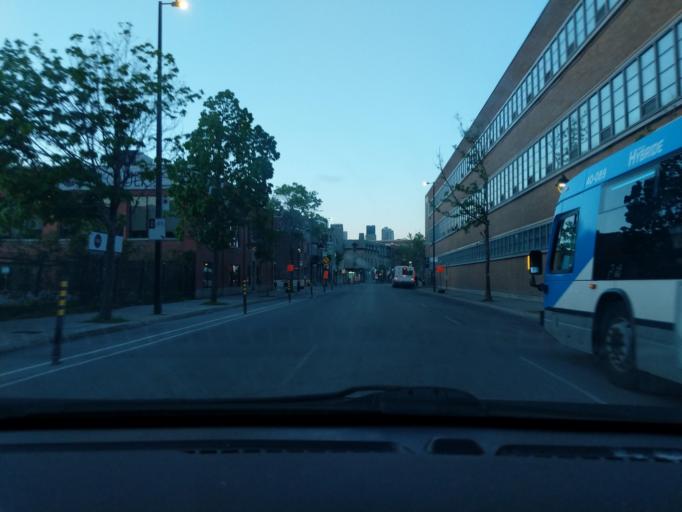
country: CA
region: Quebec
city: Westmount
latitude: 45.4818
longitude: -73.5824
